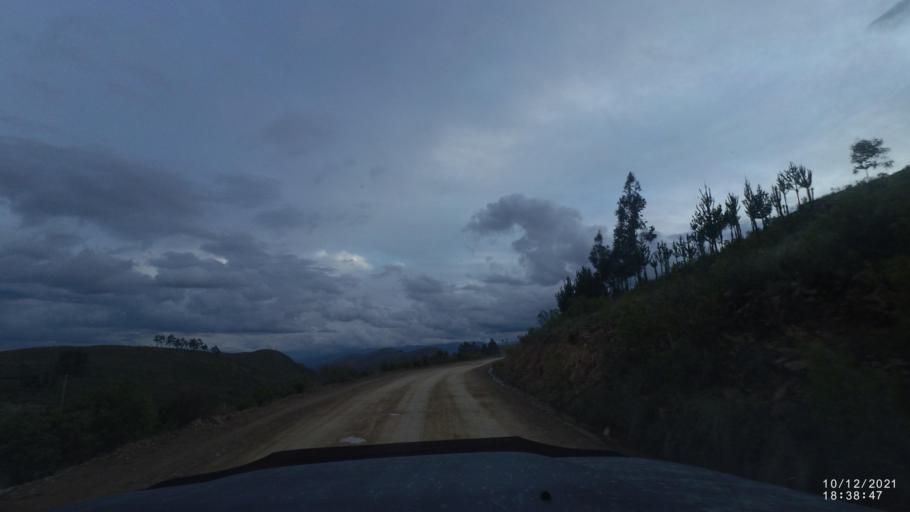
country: BO
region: Cochabamba
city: Tarata
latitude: -17.8446
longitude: -65.9896
